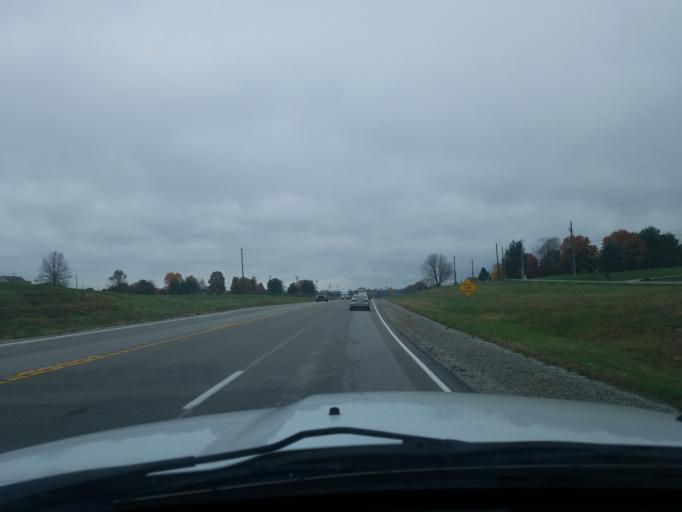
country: US
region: Kentucky
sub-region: Marion County
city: Lebanon
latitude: 37.5475
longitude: -85.3012
